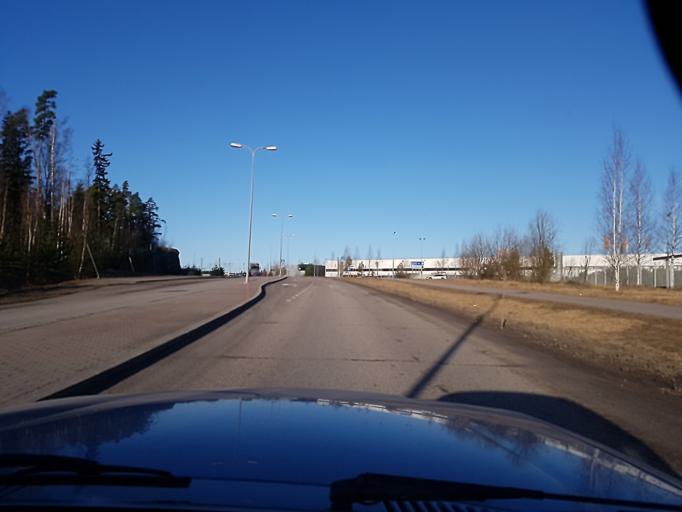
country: FI
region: Uusimaa
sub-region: Helsinki
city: Vantaa
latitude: 60.2948
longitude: 24.9189
